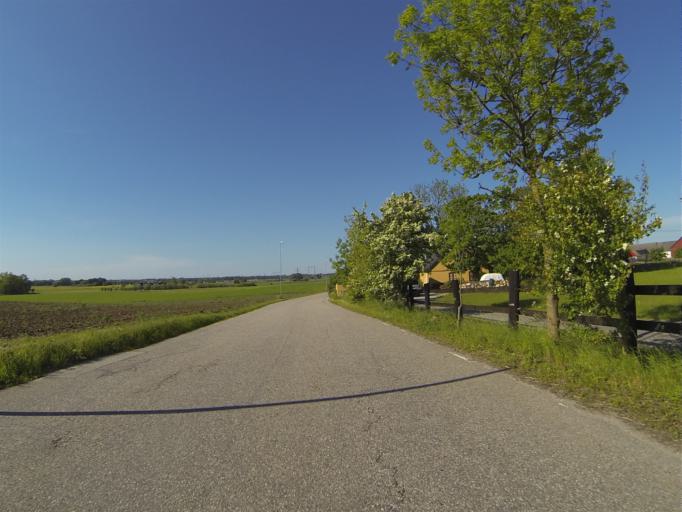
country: SE
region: Skane
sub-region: Burlovs Kommun
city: Arloev
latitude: 55.5969
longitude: 13.1329
